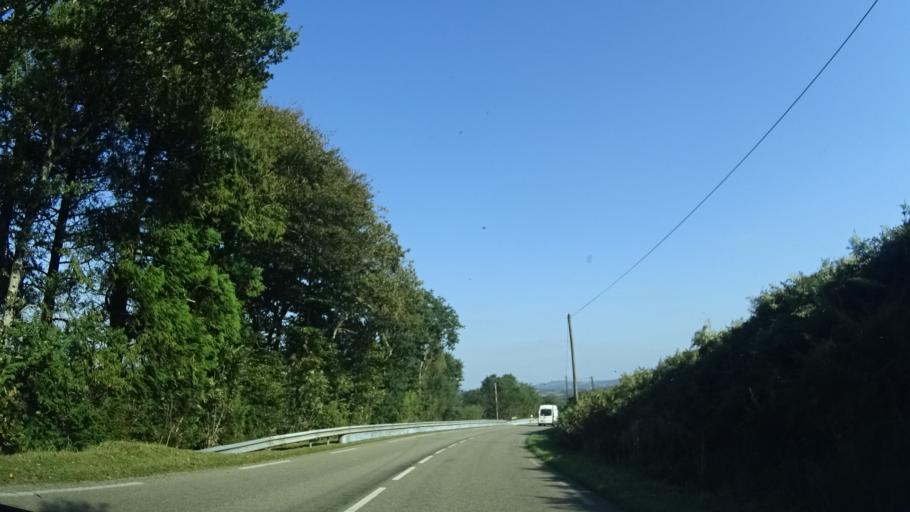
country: FR
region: Brittany
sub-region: Departement du Finistere
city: Cast
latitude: 48.1782
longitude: -4.1208
